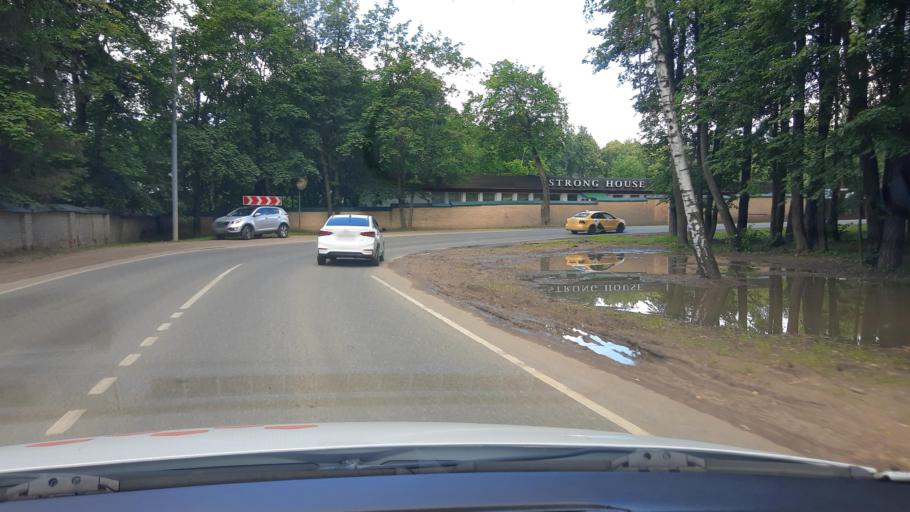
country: RU
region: Moskovskaya
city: Filimonki
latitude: 55.5703
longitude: 37.3545
